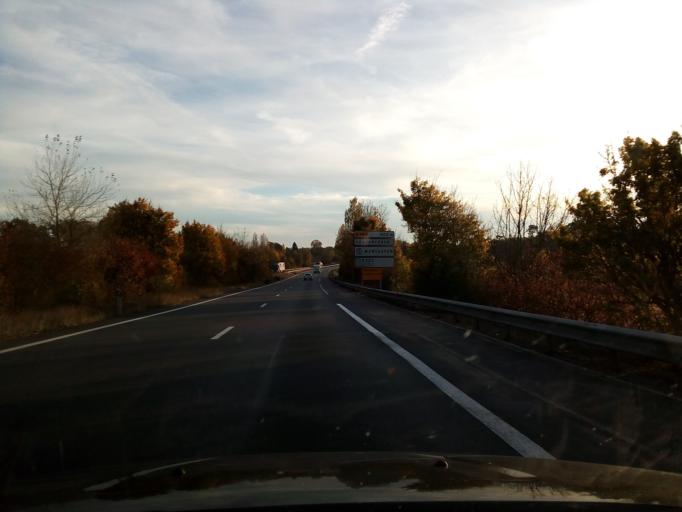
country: FR
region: Poitou-Charentes
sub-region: Departement de la Charente-Maritime
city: Chevanceaux
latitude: 45.3175
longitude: -0.2301
